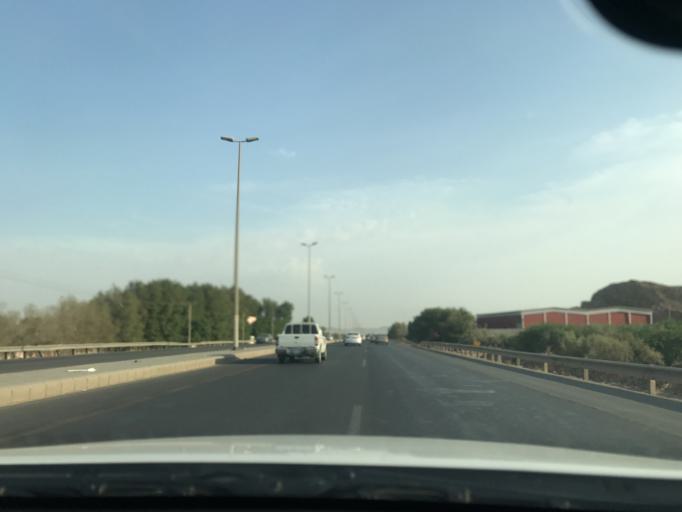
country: SA
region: Makkah
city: Jeddah
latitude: 21.4004
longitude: 39.4267
